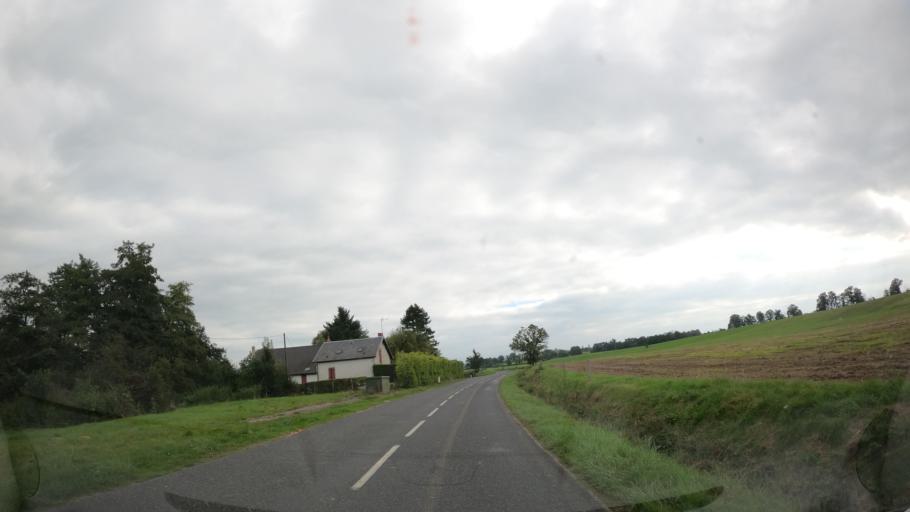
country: FR
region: Auvergne
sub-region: Departement de l'Allier
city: Lapalisse
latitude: 46.3205
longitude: 3.6334
